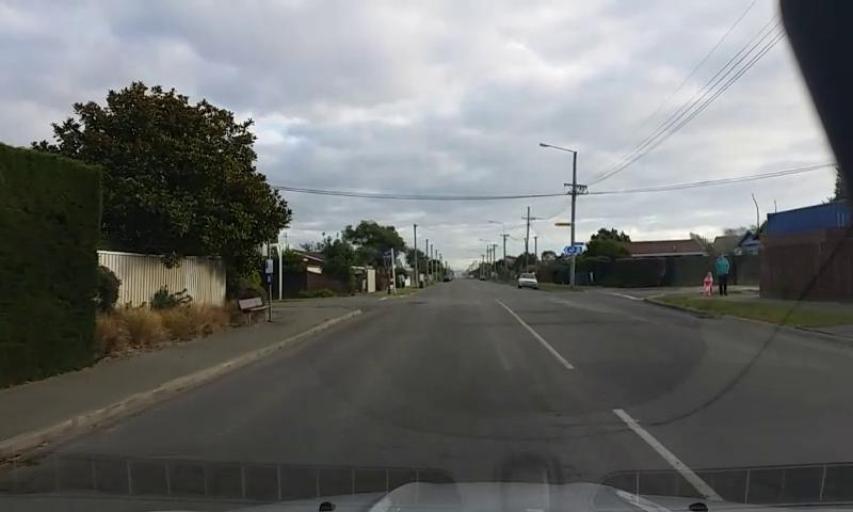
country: NZ
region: Canterbury
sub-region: Christchurch City
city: Christchurch
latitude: -43.5345
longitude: 172.7375
